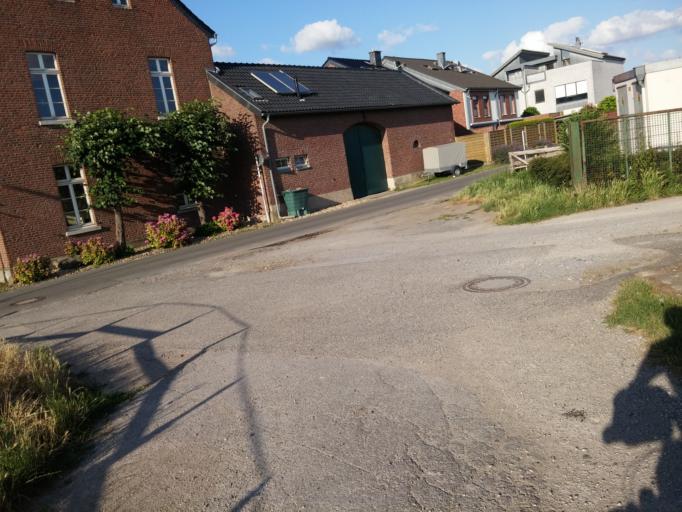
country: DE
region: North Rhine-Westphalia
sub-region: Regierungsbezirk Dusseldorf
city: Korschenbroich
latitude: 51.1496
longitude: 6.5175
